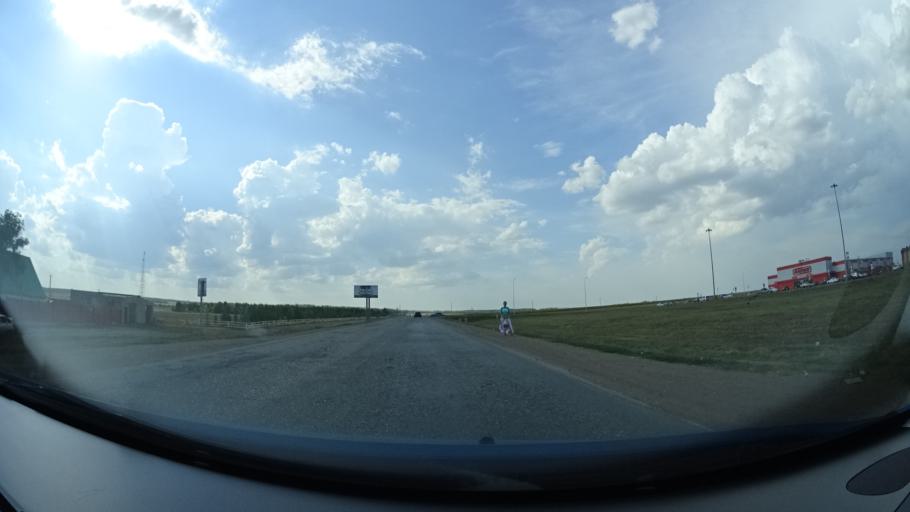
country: RU
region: Bashkortostan
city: Meleuz
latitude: 52.9647
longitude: 55.9094
